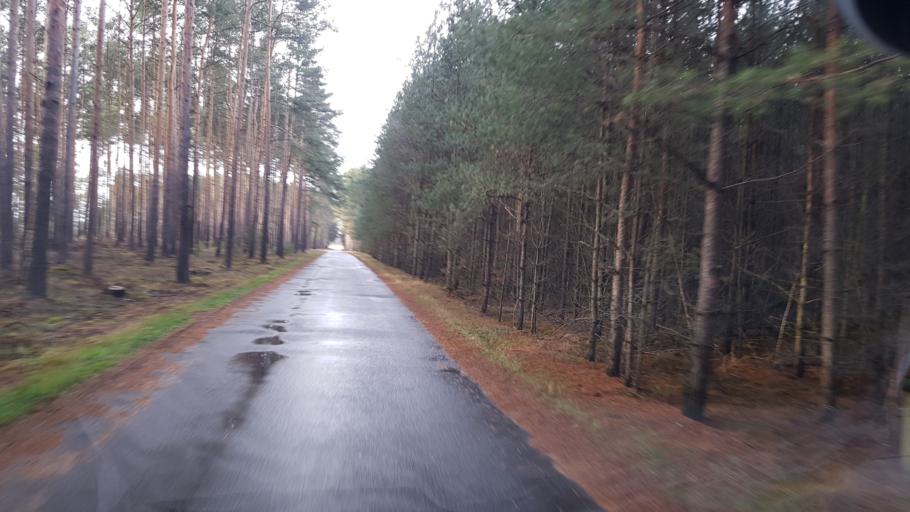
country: DE
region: Brandenburg
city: Bronkow
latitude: 51.6659
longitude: 13.8786
